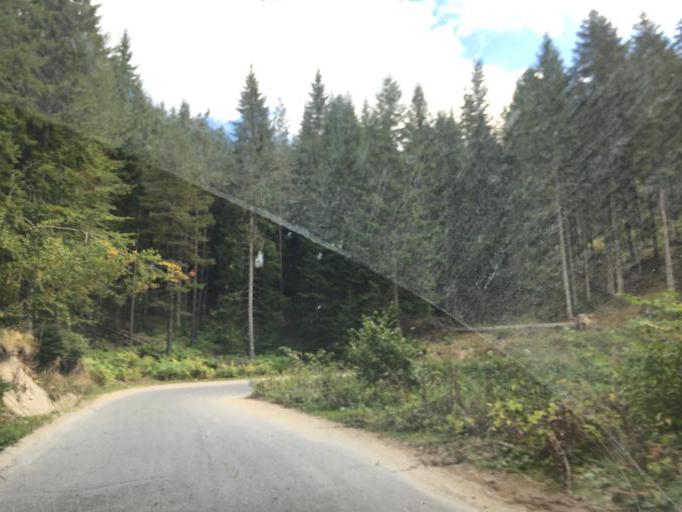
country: BG
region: Pazardzhik
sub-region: Obshtina Batak
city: Batak
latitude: 41.9112
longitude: 24.2903
